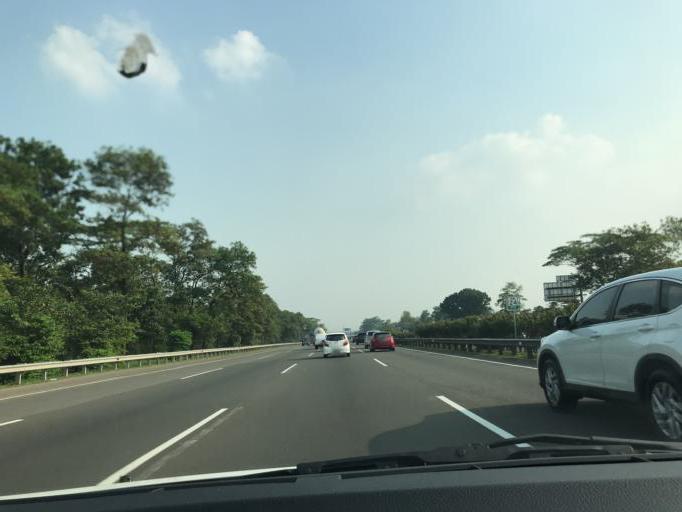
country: ID
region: West Java
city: Citeureup
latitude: -6.4632
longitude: 106.8840
